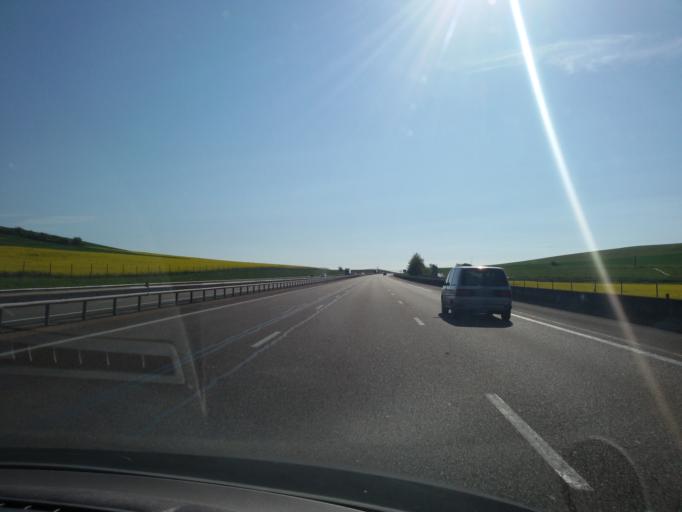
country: FR
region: Bourgogne
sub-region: Departement de l'Yonne
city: Aillant-sur-Tholon
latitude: 47.8978
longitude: 3.3760
